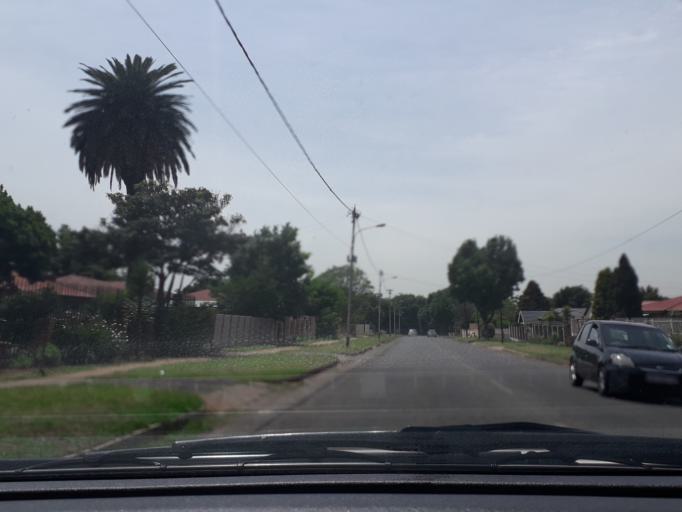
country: ZA
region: Gauteng
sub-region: City of Johannesburg Metropolitan Municipality
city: Roodepoort
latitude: -26.1820
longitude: 27.9248
